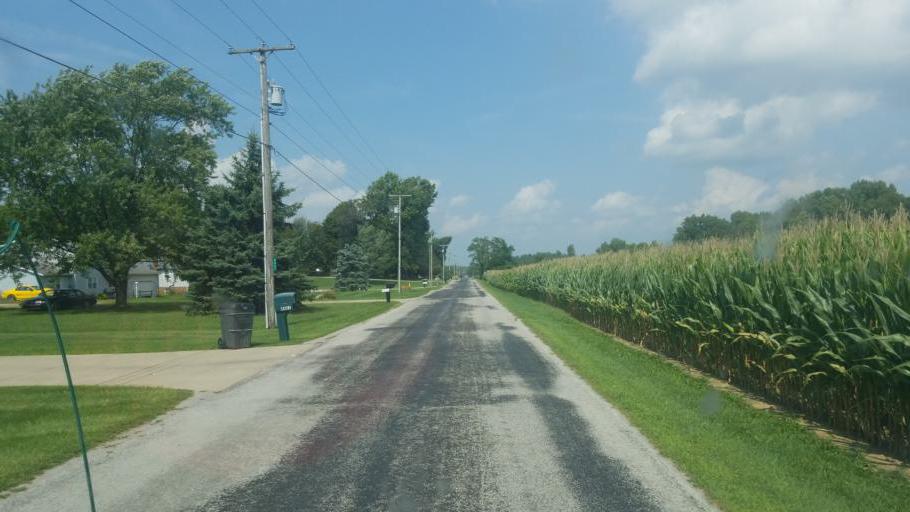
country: US
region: Ohio
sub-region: Richland County
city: Shelby
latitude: 40.8763
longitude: -82.5956
